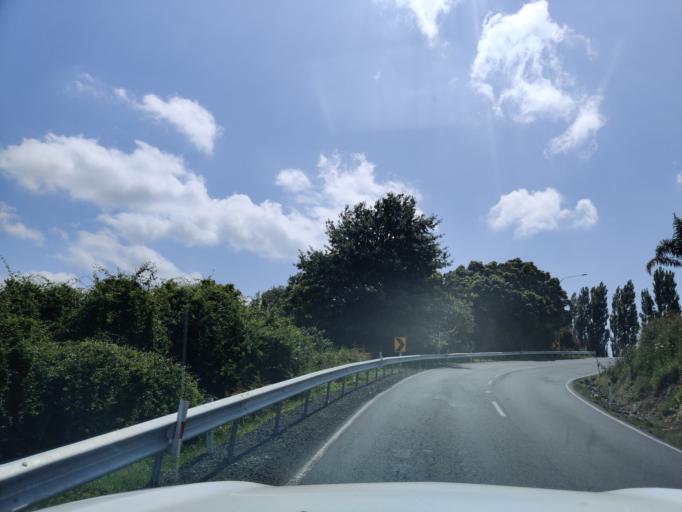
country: NZ
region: Auckland
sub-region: Auckland
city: Pukekohe East
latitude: -37.2143
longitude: 174.9472
